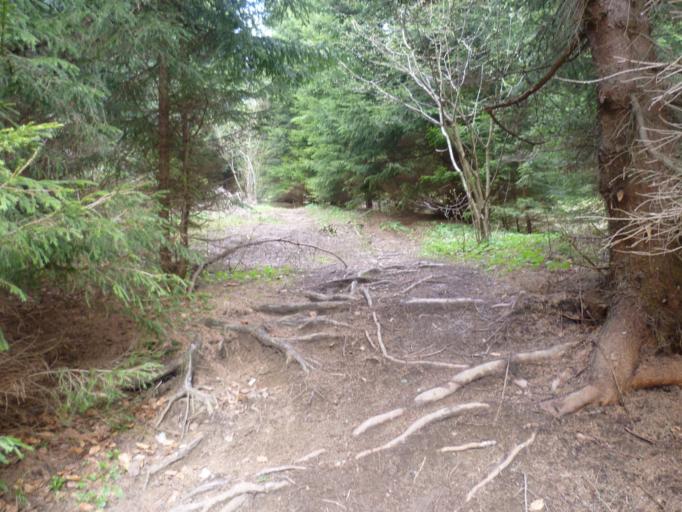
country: SK
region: Zilinsky
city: Ruzomberok
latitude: 49.1368
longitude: 19.3705
